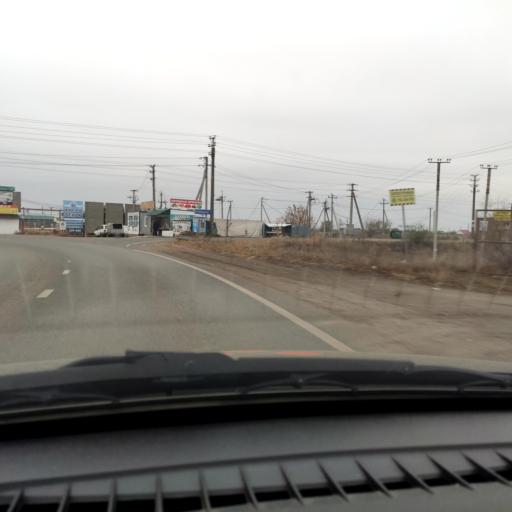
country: RU
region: Samara
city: Podstepki
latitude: 53.5235
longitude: 49.1969
